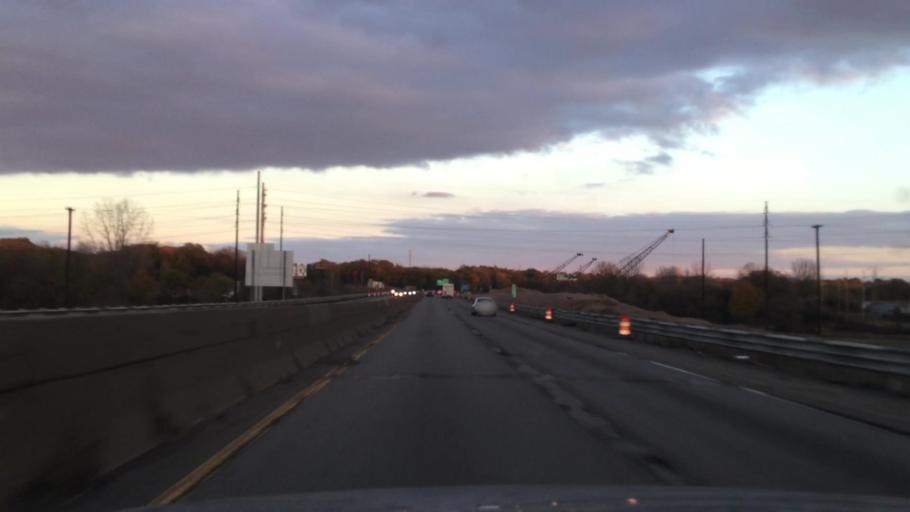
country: US
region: Michigan
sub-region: Jackson County
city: Jackson
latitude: 42.2720
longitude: -84.4132
